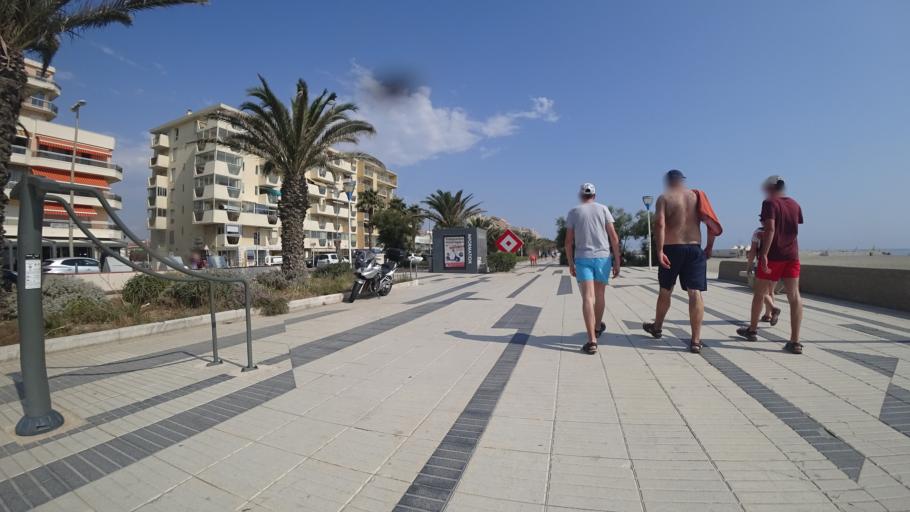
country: FR
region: Languedoc-Roussillon
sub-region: Departement des Pyrenees-Orientales
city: Canet-en-Roussillon
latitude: 42.6834
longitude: 3.0346
